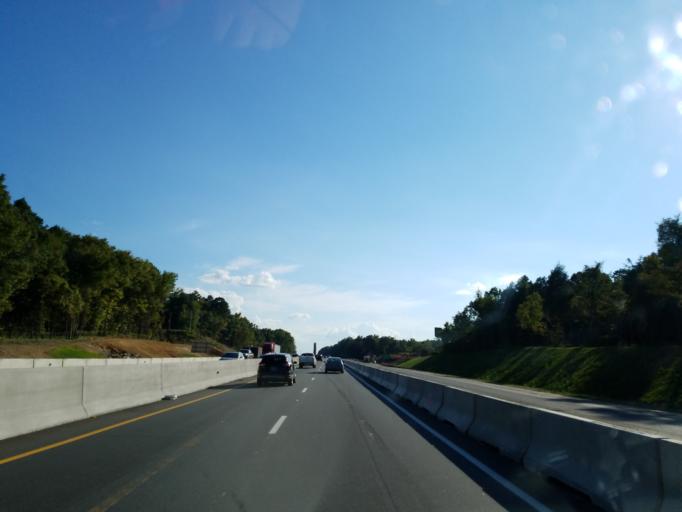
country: US
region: North Carolina
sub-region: Cabarrus County
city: Kannapolis
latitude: 35.4925
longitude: -80.5683
